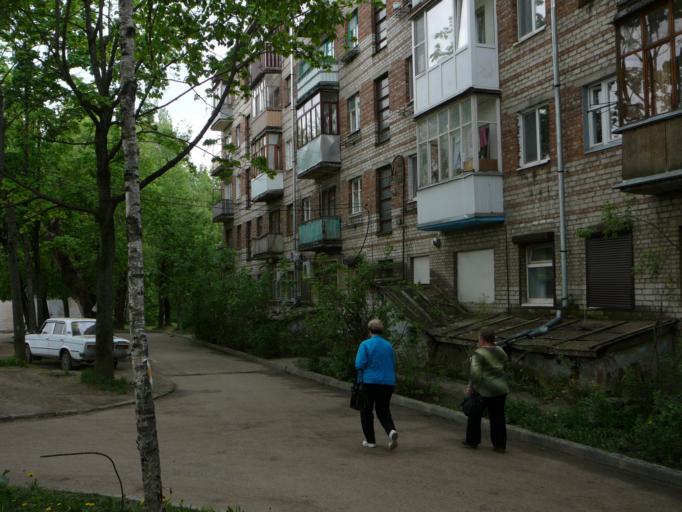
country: RU
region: Smolensk
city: Smolensk
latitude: 54.7728
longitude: 32.0320
